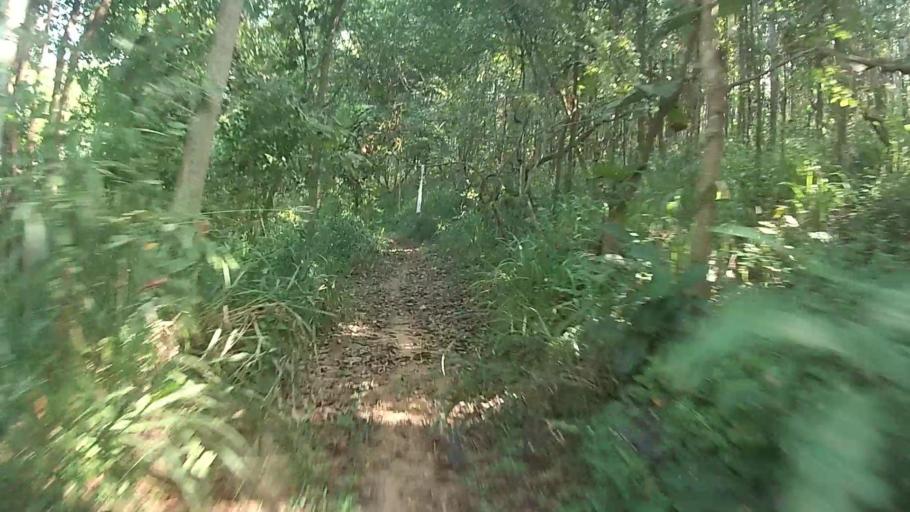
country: TH
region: Chiang Mai
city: San Sai
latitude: 18.9288
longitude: 99.0602
